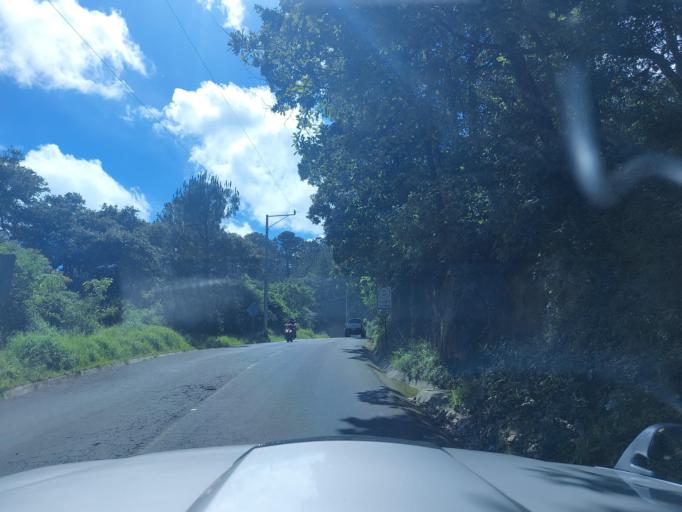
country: GT
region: Chimaltenango
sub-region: Municipio de San Juan Comalapa
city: Comalapa
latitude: 14.7121
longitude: -90.8911
